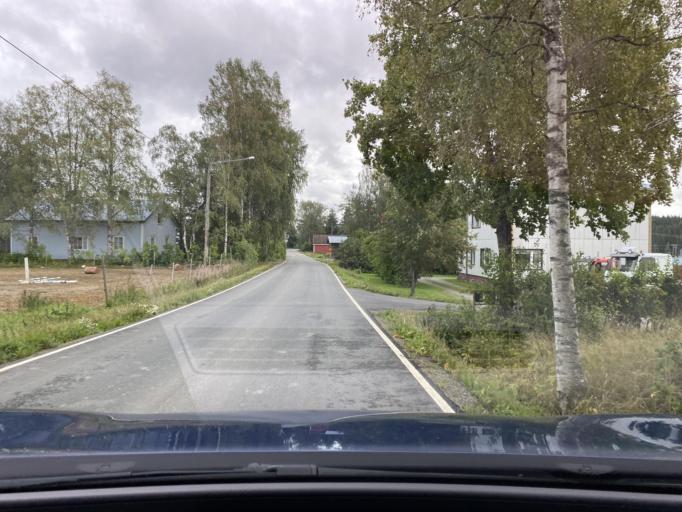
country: FI
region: Pirkanmaa
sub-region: Lounais-Pirkanmaa
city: Punkalaidun
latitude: 61.1666
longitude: 23.1835
